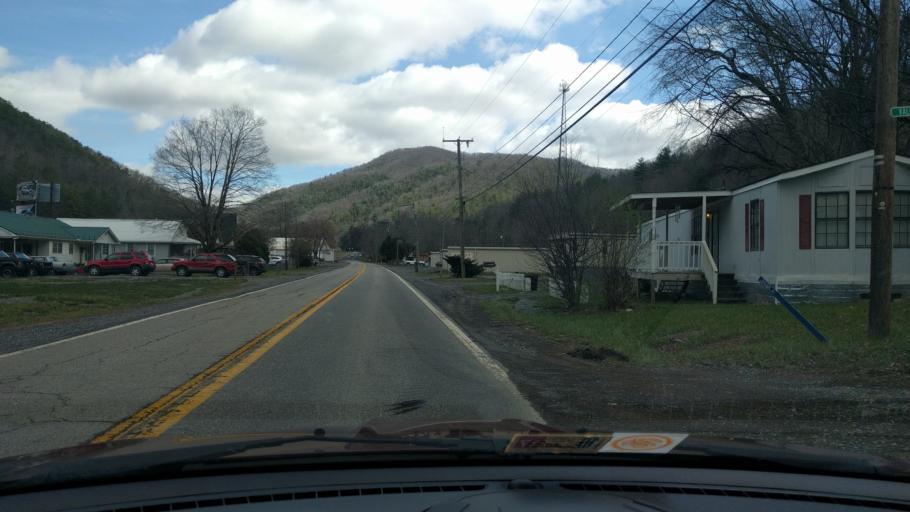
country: US
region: West Virginia
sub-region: Greenbrier County
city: White Sulphur Springs
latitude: 37.7944
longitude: -80.2753
